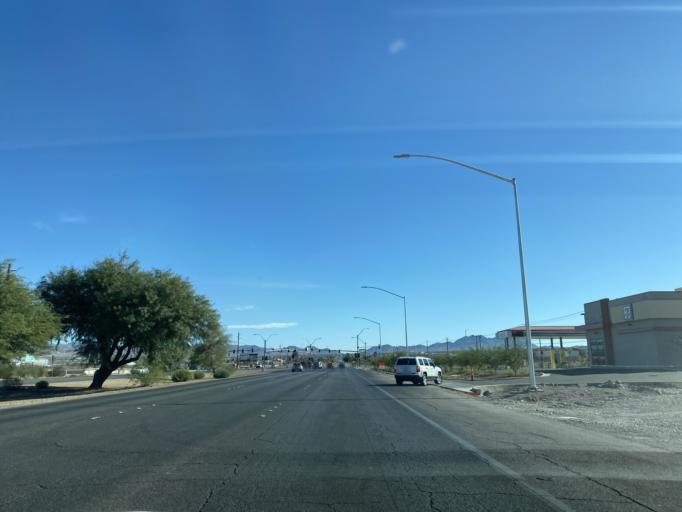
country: US
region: Nevada
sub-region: Clark County
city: Henderson
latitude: 36.0723
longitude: -115.0191
